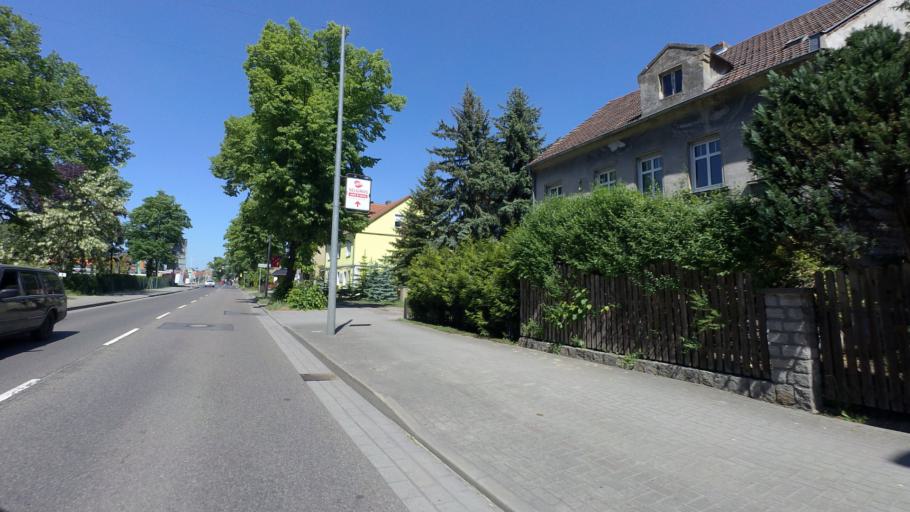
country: DE
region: Brandenburg
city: Cottbus
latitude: 51.7193
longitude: 14.3479
